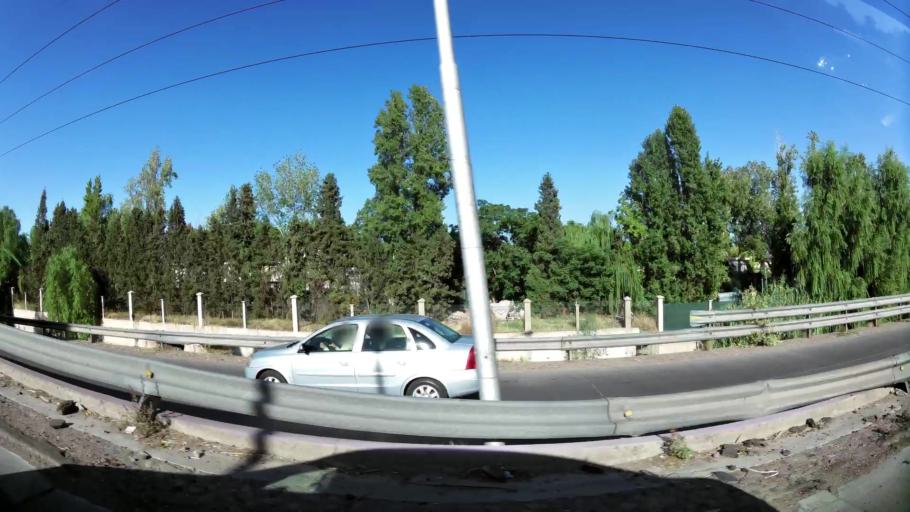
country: AR
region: Mendoza
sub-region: Departamento de Godoy Cruz
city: Godoy Cruz
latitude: -32.9121
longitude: -68.8384
